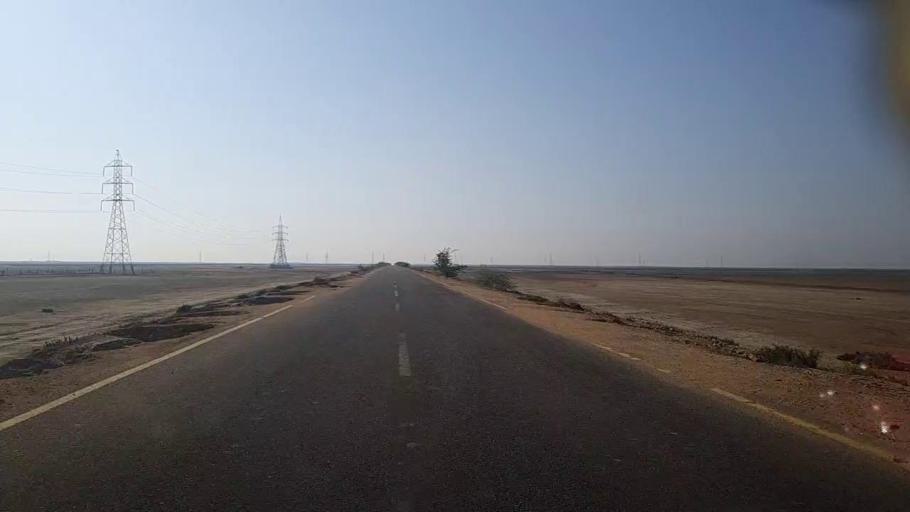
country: PK
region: Sindh
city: Mirpur Sakro
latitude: 24.6038
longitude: 67.4976
